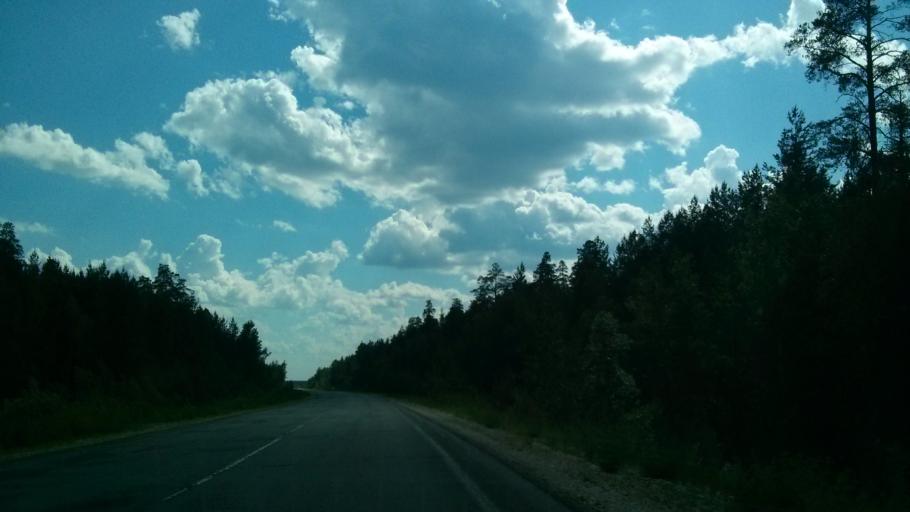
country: RU
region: Vladimir
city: Melenki
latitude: 55.3510
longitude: 41.6765
